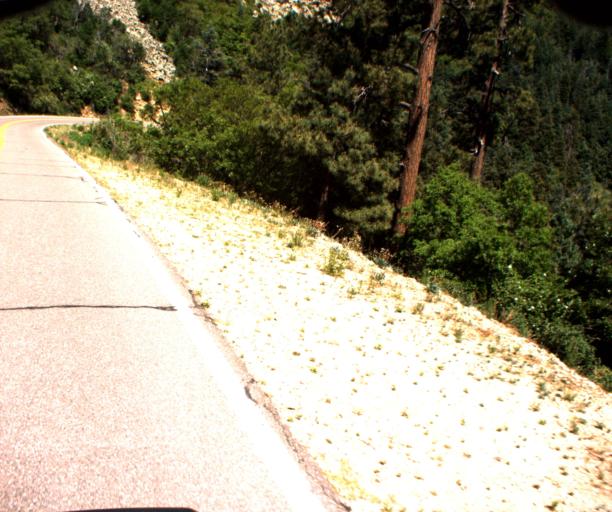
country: US
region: Arizona
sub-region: Graham County
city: Swift Trail Junction
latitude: 32.6438
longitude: -109.8517
